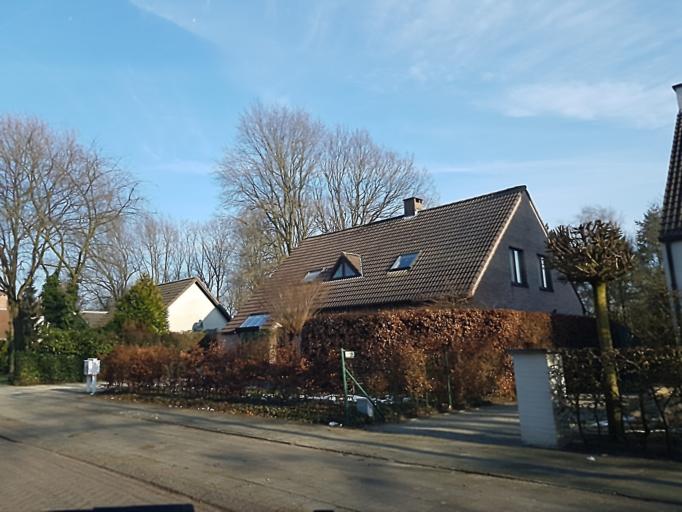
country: BE
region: Flanders
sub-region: Provincie Antwerpen
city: Brasschaat
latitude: 51.3171
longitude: 4.5193
